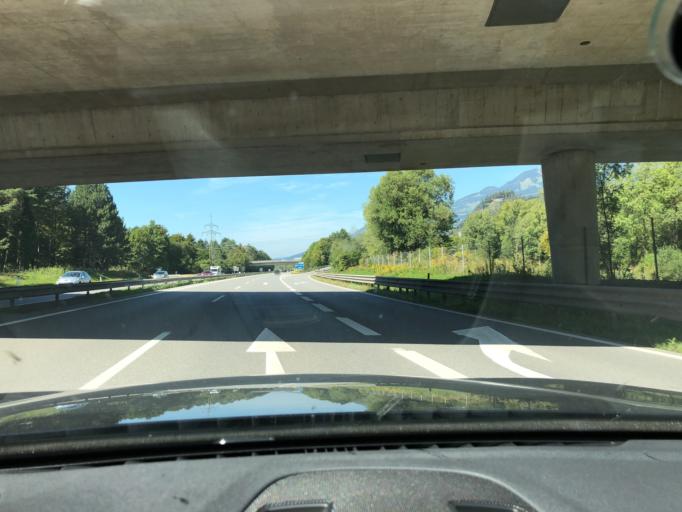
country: AT
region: Vorarlberg
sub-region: Politischer Bezirk Bludenz
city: Nuziders
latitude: 47.1654
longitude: 9.7921
